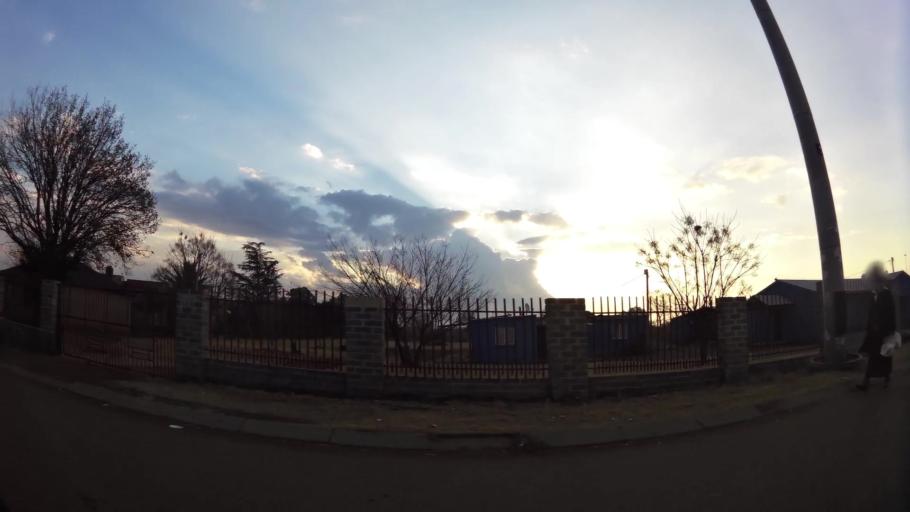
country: ZA
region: Gauteng
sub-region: City of Johannesburg Metropolitan Municipality
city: Orange Farm
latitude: -26.5391
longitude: 27.8496
